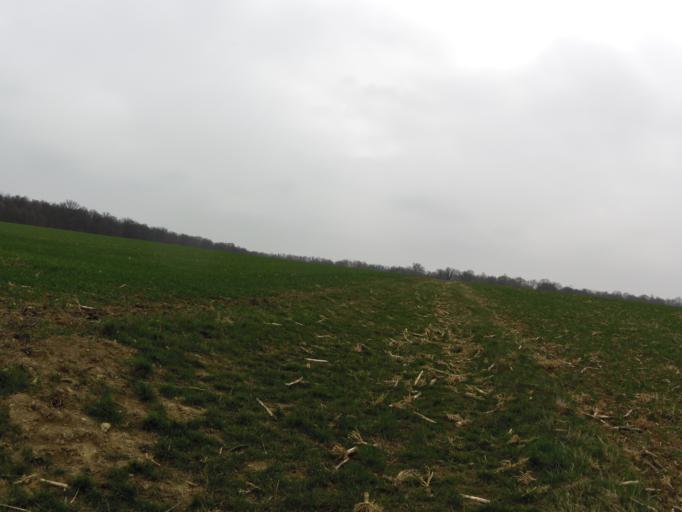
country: DE
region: Bavaria
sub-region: Regierungsbezirk Unterfranken
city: Rottendorf
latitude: 49.8211
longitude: 10.0372
